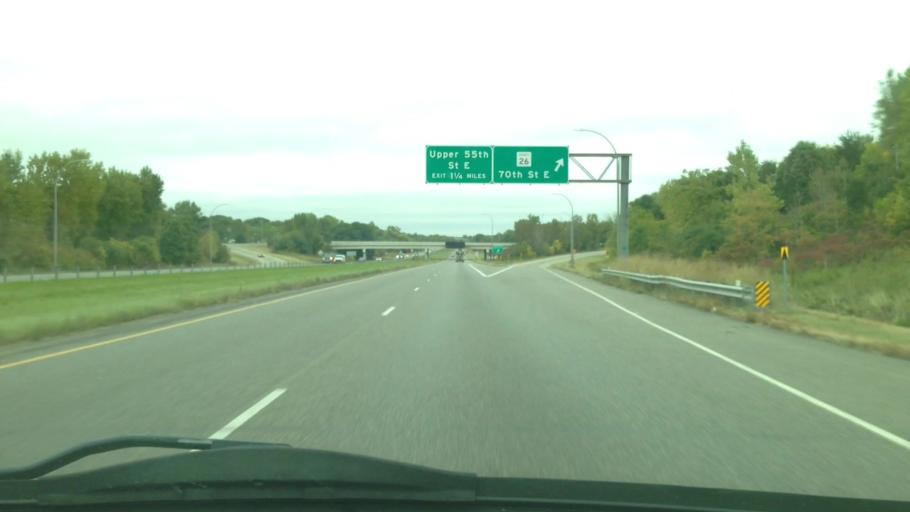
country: US
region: Minnesota
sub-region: Dakota County
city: Inver Grove Heights
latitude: 44.8436
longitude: -93.0595
